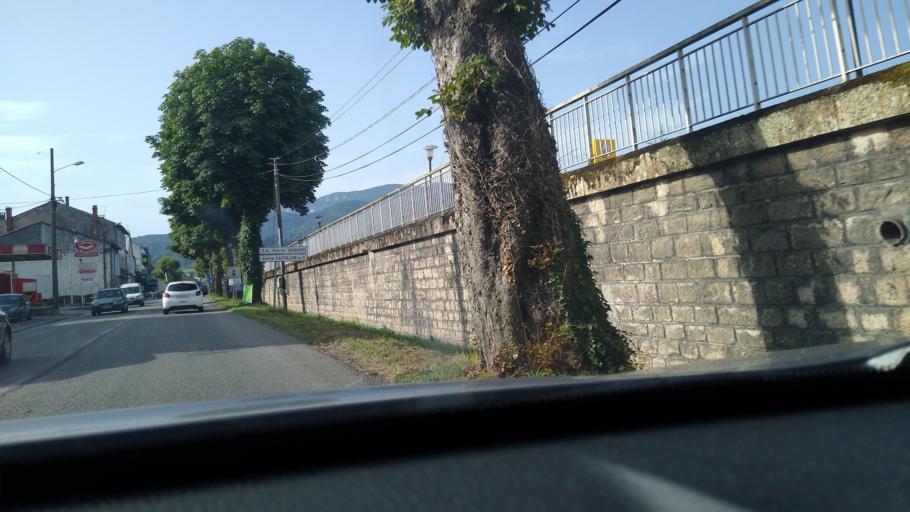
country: FR
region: Midi-Pyrenees
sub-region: Departement de l'Ariege
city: Saint-Girons
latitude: 42.9895
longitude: 1.1391
